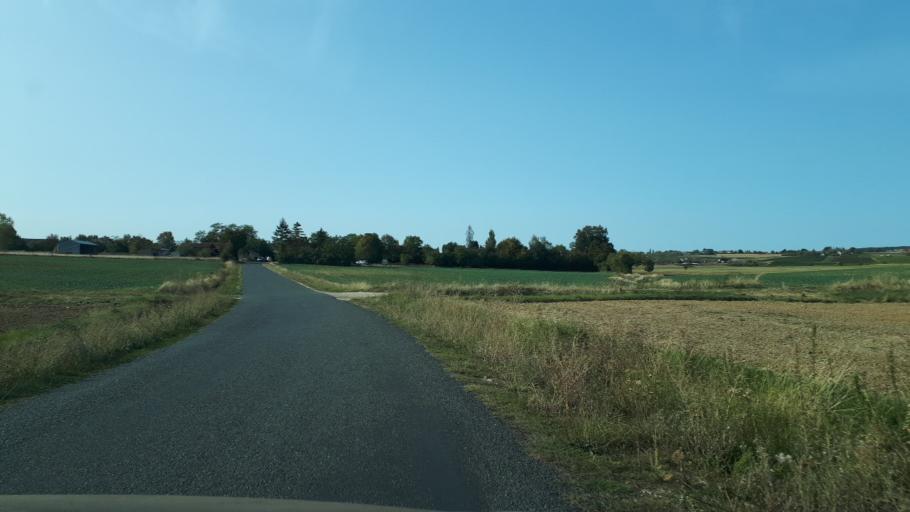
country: FR
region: Centre
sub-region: Departement du Cher
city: Menetou-Salon
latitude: 47.2145
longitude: 2.5514
